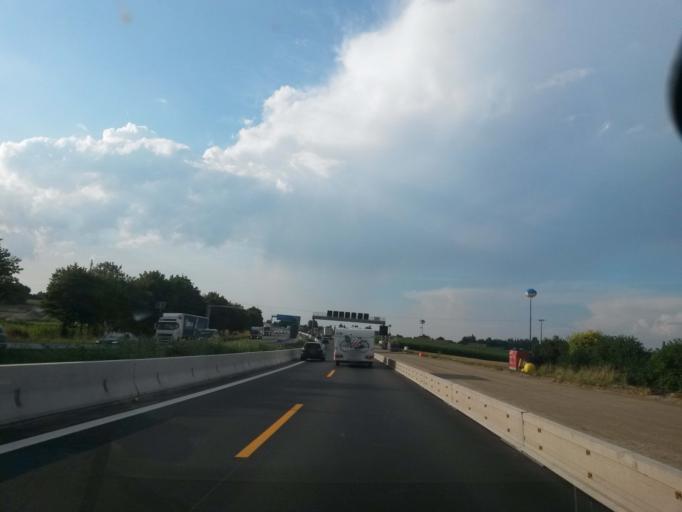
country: DE
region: Bavaria
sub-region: Upper Bavaria
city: Schweitenkirchen
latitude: 48.4961
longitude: 11.5949
